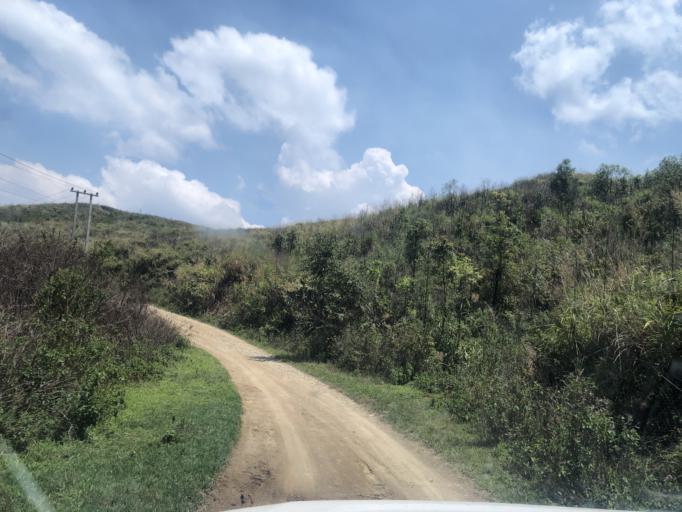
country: LA
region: Phongsali
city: Phongsali
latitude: 21.4035
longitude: 102.1861
